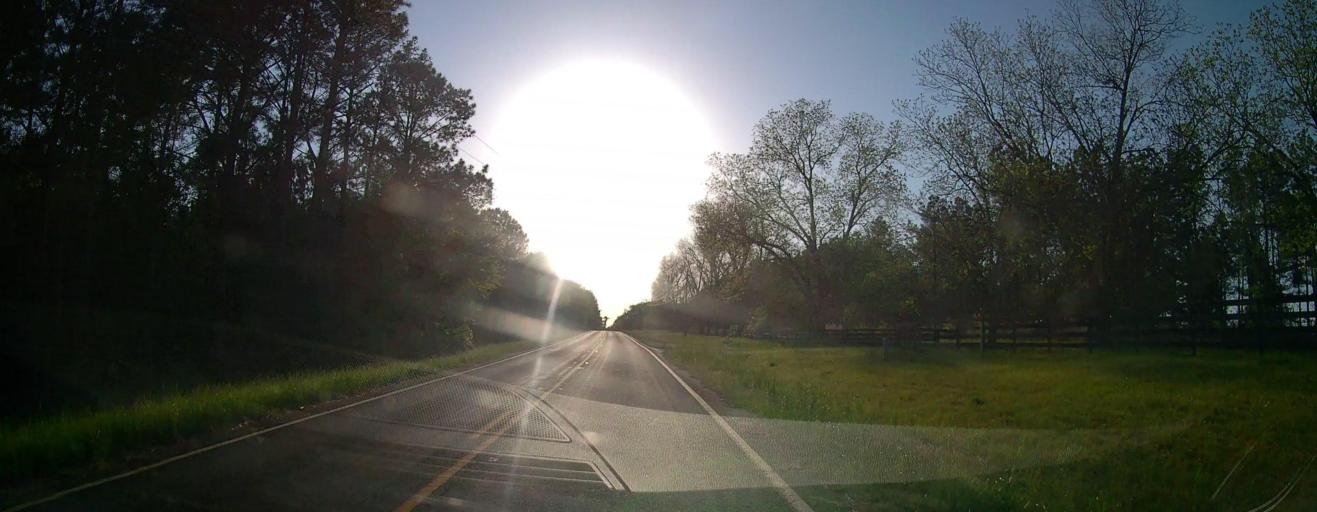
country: US
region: Georgia
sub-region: Macon County
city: Oglethorpe
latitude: 32.3198
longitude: -84.1943
